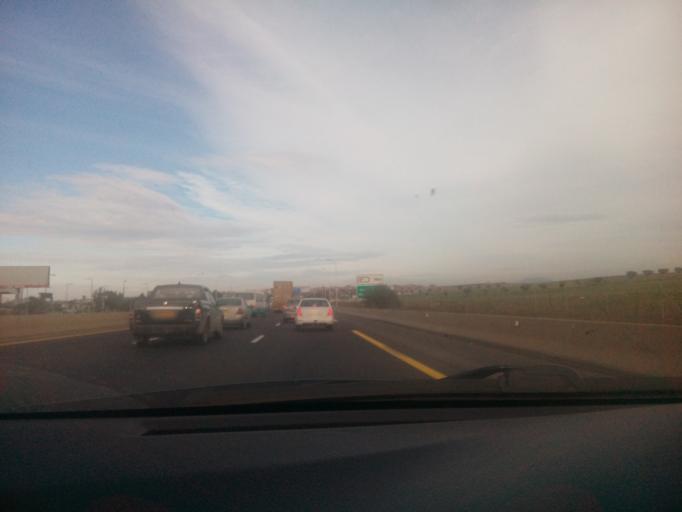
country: DZ
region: Oran
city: Es Senia
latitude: 35.5917
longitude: -0.5719
